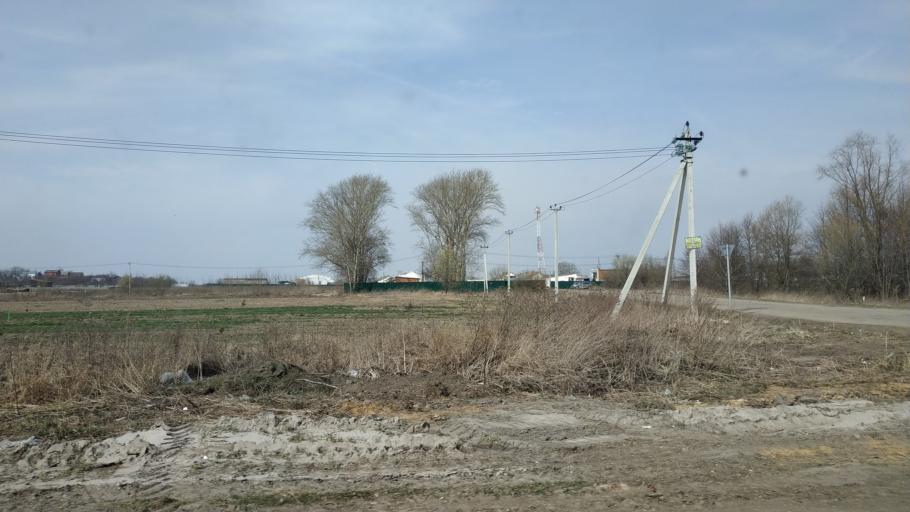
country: RU
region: Moskovskaya
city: Troitskoye
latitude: 55.3542
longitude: 38.5001
